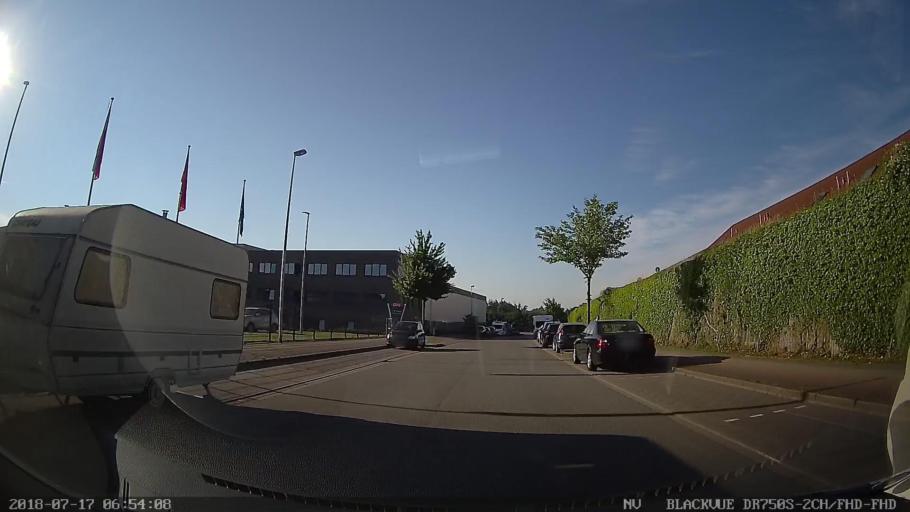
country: DE
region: Schleswig-Holstein
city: Rellingen
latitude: 53.6459
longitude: 9.8235
